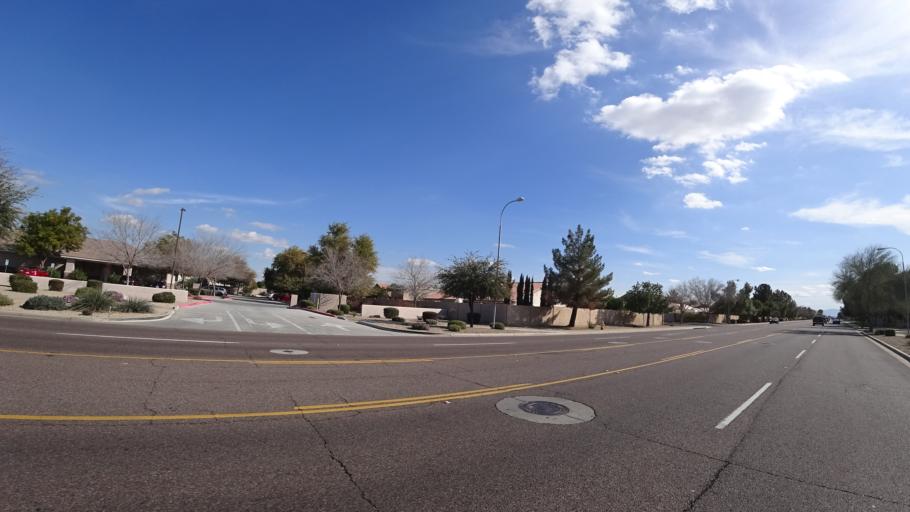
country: US
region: Arizona
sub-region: Maricopa County
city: Peoria
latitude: 33.6233
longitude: -112.2201
